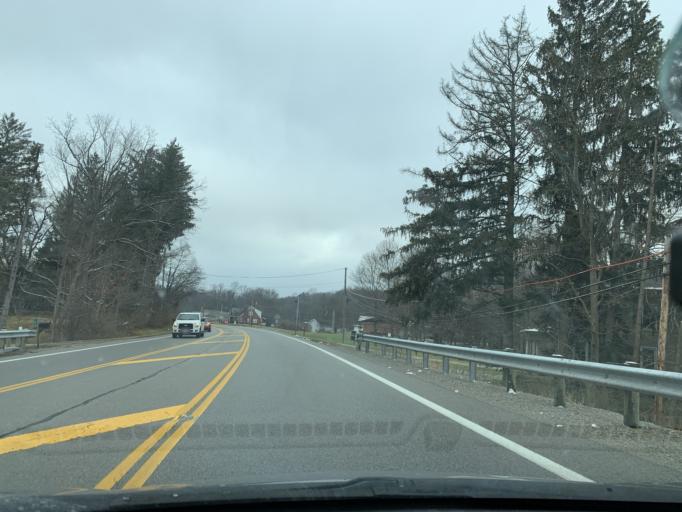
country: US
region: Ohio
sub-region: Licking County
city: Granville South
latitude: 40.0553
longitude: -82.5362
